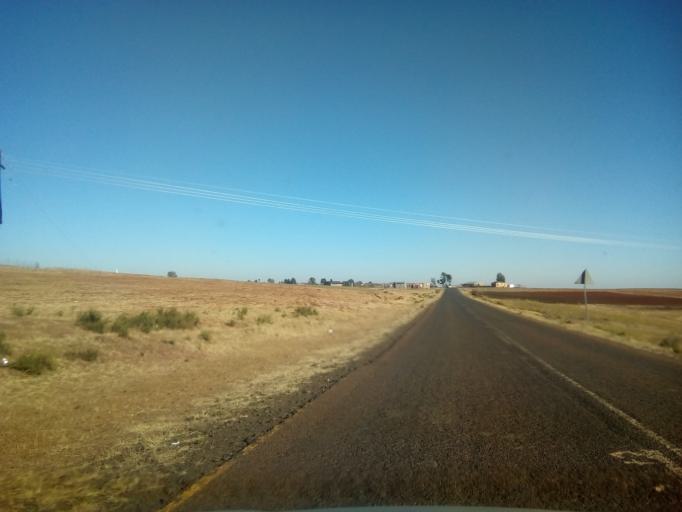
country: LS
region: Berea
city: Teyateyaneng
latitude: -29.2523
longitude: 27.7384
